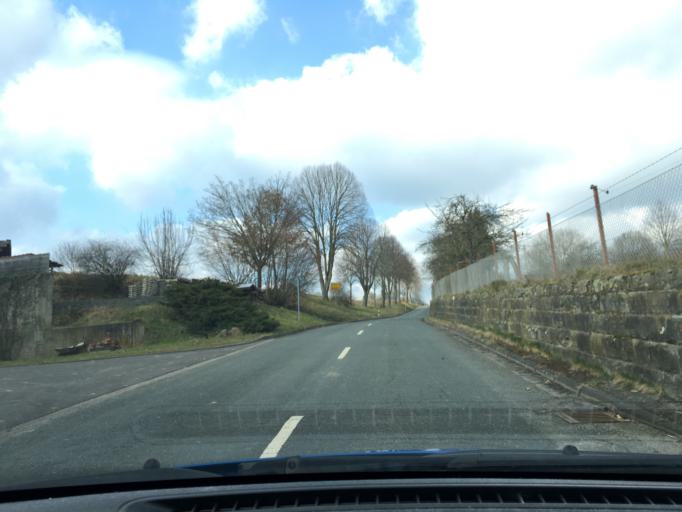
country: DE
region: Lower Saxony
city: Uslar
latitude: 51.6024
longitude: 9.6386
